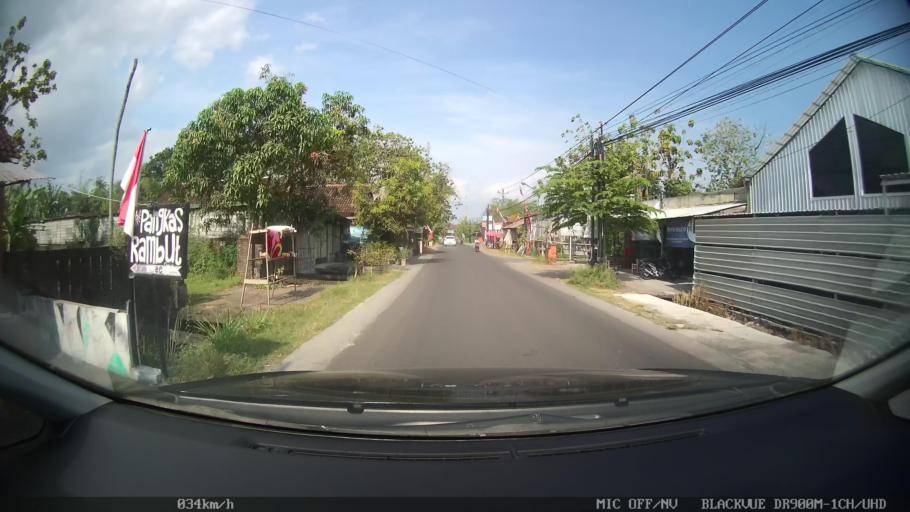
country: ID
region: Daerah Istimewa Yogyakarta
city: Kasihan
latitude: -7.8417
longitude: 110.3293
